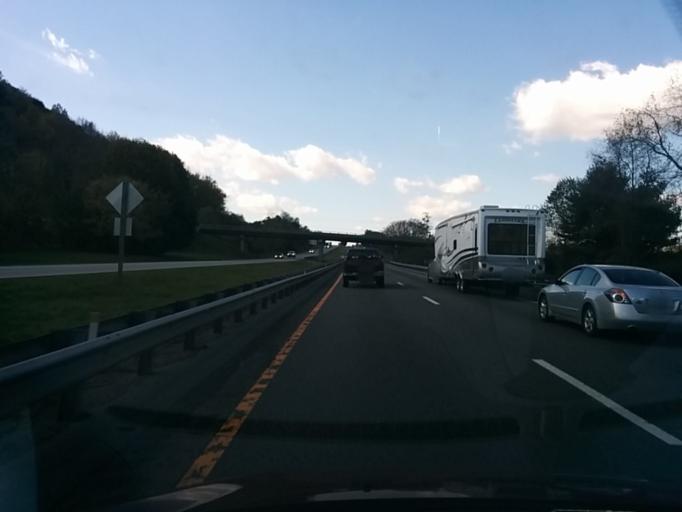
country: US
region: Virginia
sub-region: Botetourt County
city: Buchanan
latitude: 37.4965
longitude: -79.7541
